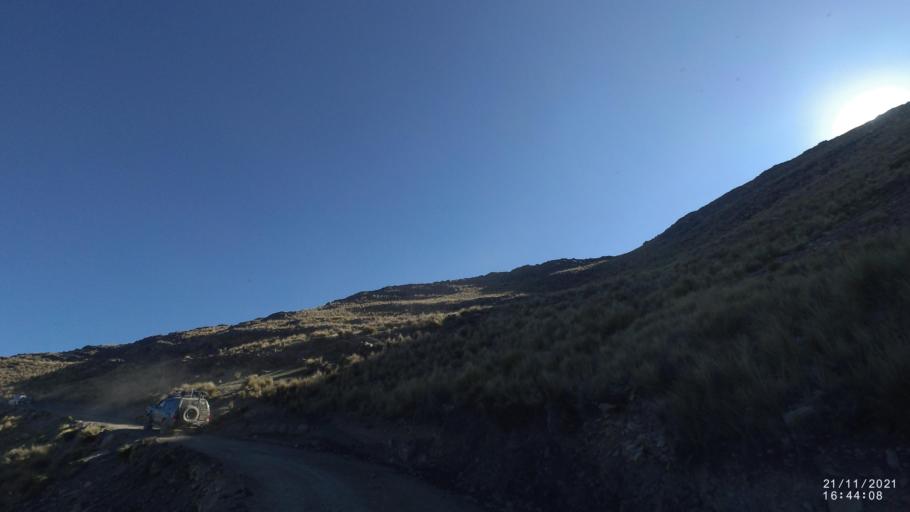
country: BO
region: Cochabamba
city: Cochabamba
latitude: -17.0728
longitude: -66.2580
